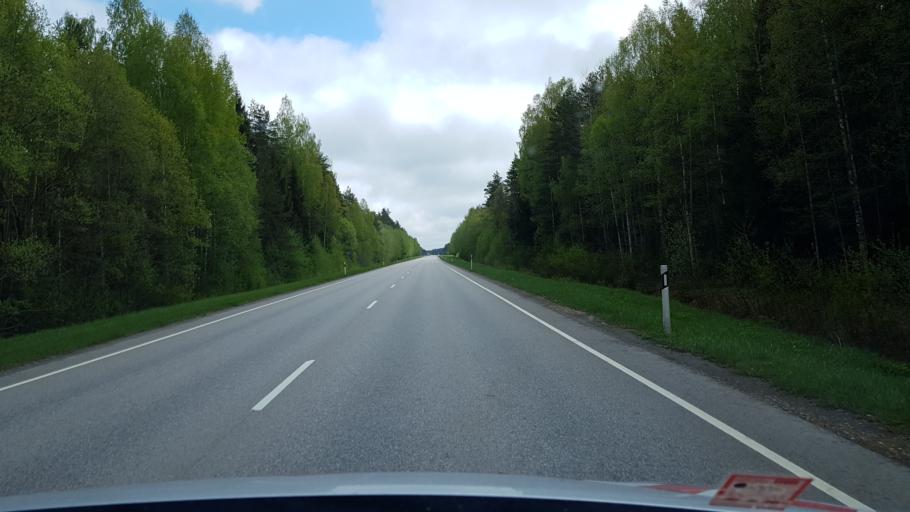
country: EE
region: Paernumaa
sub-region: Saarde vald
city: Kilingi-Nomme
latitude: 58.1535
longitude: 24.9137
